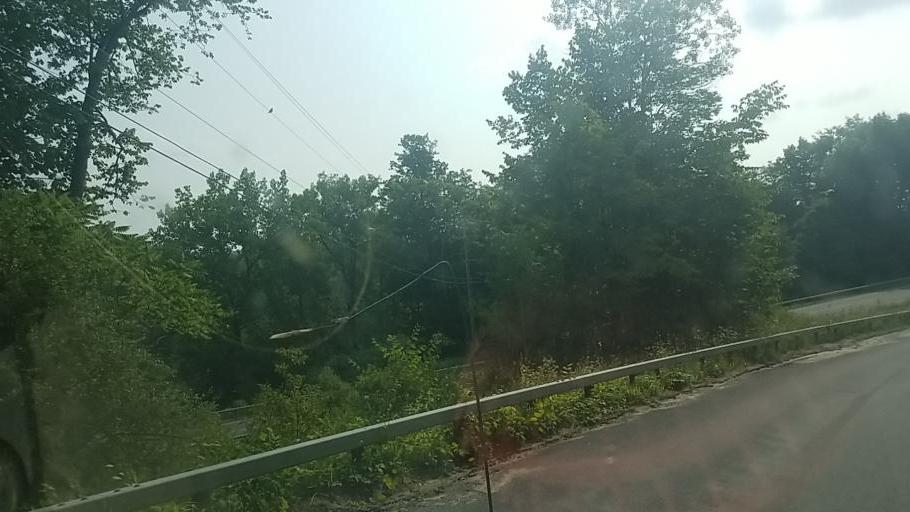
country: US
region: New York
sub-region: Montgomery County
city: Fonda
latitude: 42.9670
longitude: -74.4205
